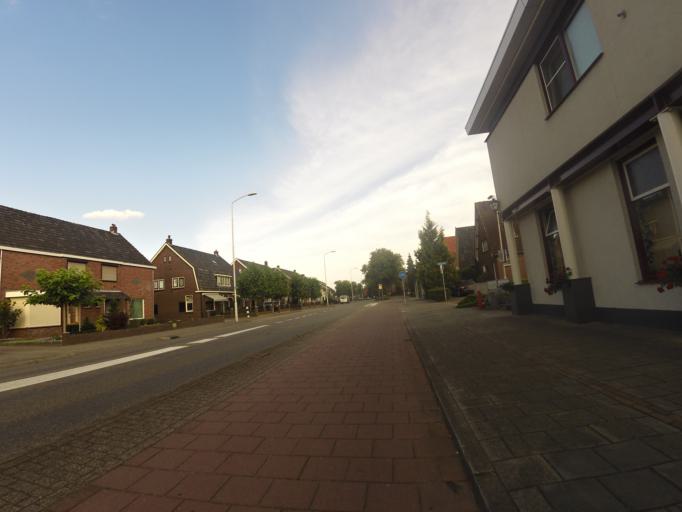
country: NL
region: Gelderland
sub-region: Oude IJsselstreek
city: Gendringen
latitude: 51.9266
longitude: 6.3531
